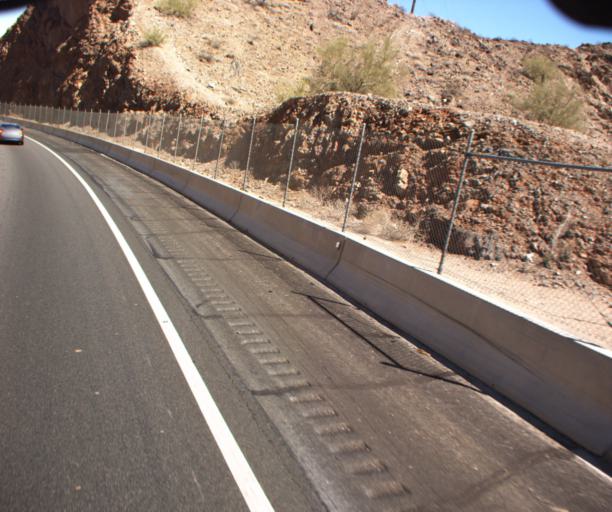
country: US
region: Arizona
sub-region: Yuma County
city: Fortuna Foothills
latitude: 32.6626
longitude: -114.3210
